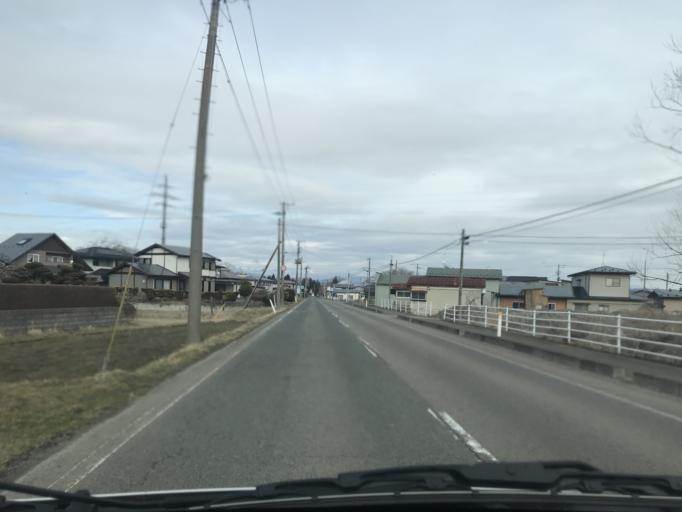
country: JP
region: Iwate
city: Hanamaki
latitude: 39.3732
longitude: 141.0986
